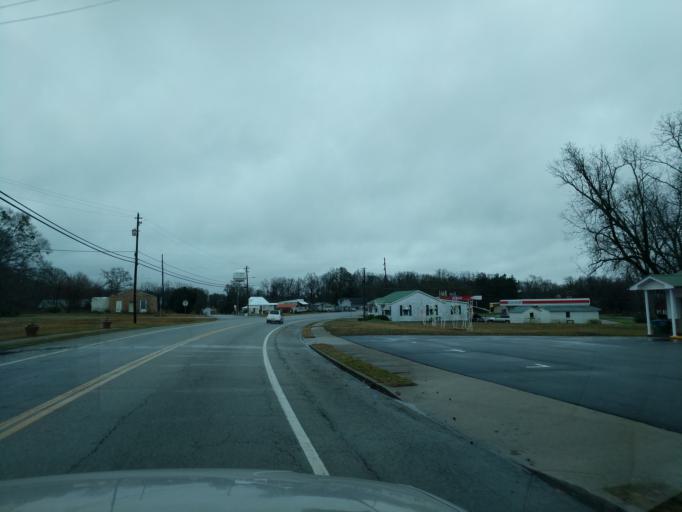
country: US
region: Georgia
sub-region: Hart County
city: Royston
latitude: 34.3448
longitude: -83.1099
